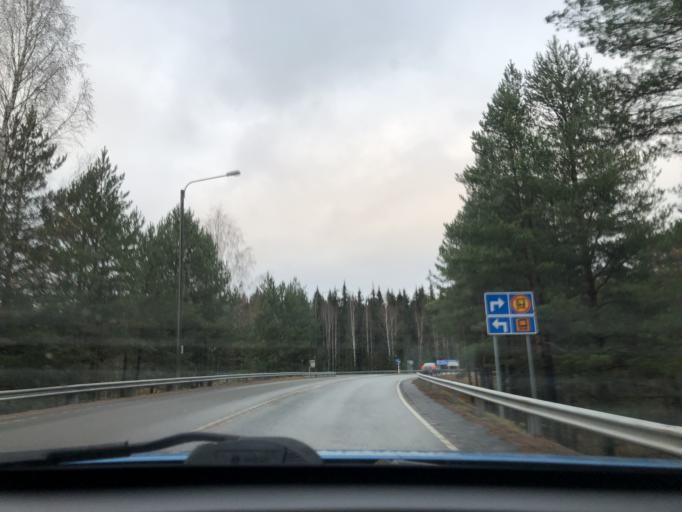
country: FI
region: Pirkanmaa
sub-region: Tampere
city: Kangasala
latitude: 61.5326
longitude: 23.9488
